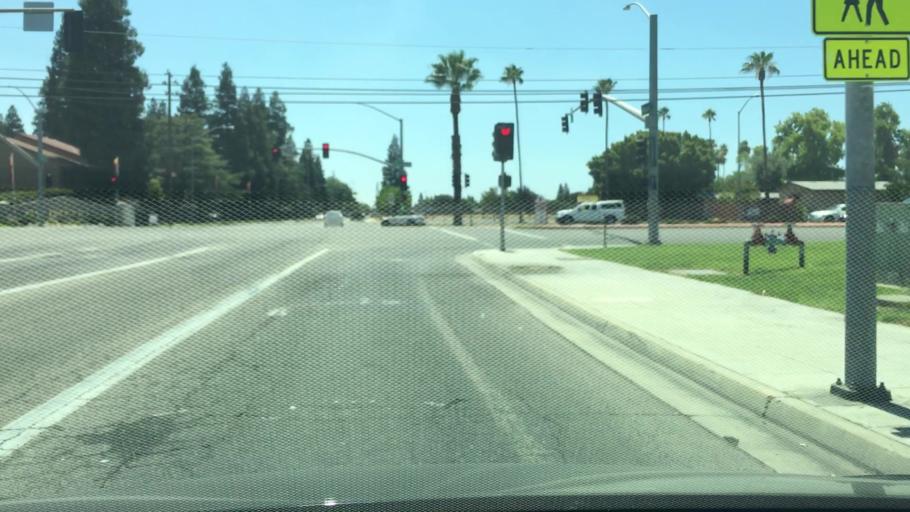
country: US
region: California
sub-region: Fresno County
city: Clovis
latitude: 36.8381
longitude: -119.7453
